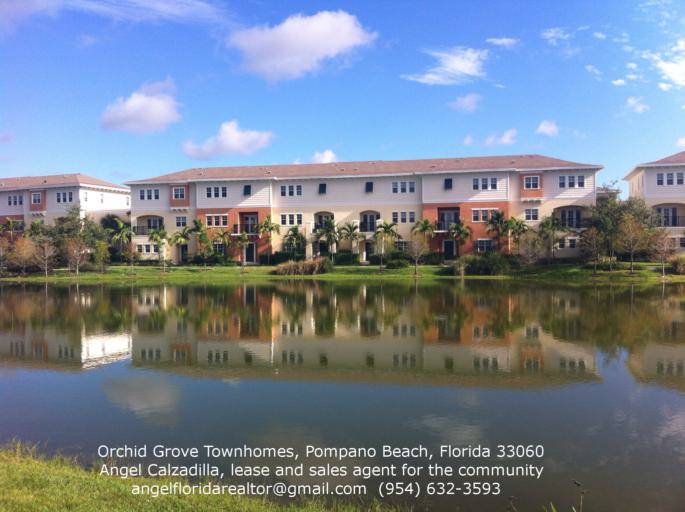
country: US
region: Florida
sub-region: Broward County
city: Pompano Beach
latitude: 26.2210
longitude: -80.1267
